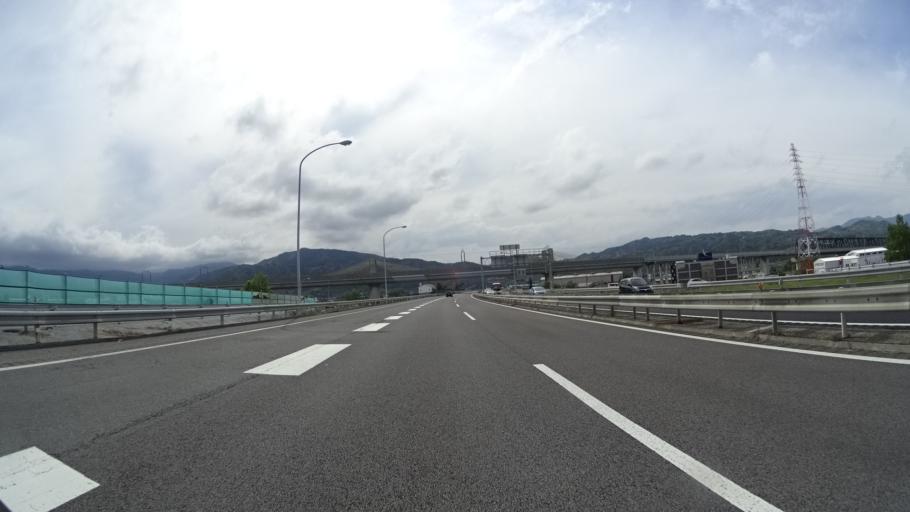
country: JP
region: Nagano
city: Nagano-shi
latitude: 36.5520
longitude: 138.1333
